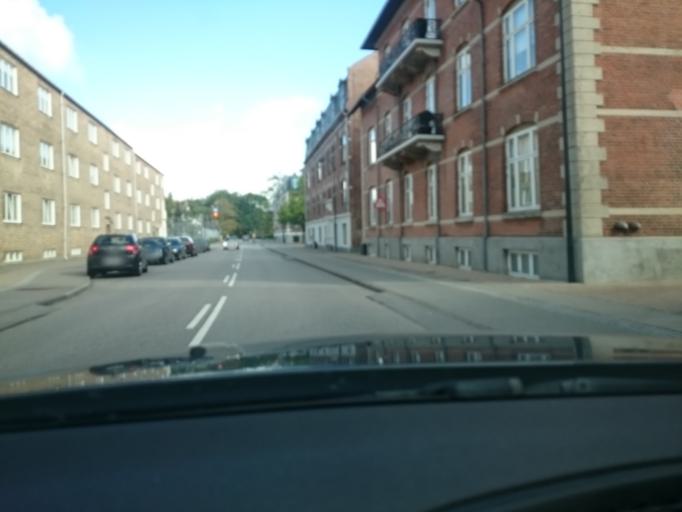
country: DK
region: Capital Region
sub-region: Gentofte Kommune
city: Charlottenlund
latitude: 55.7577
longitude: 12.5758
